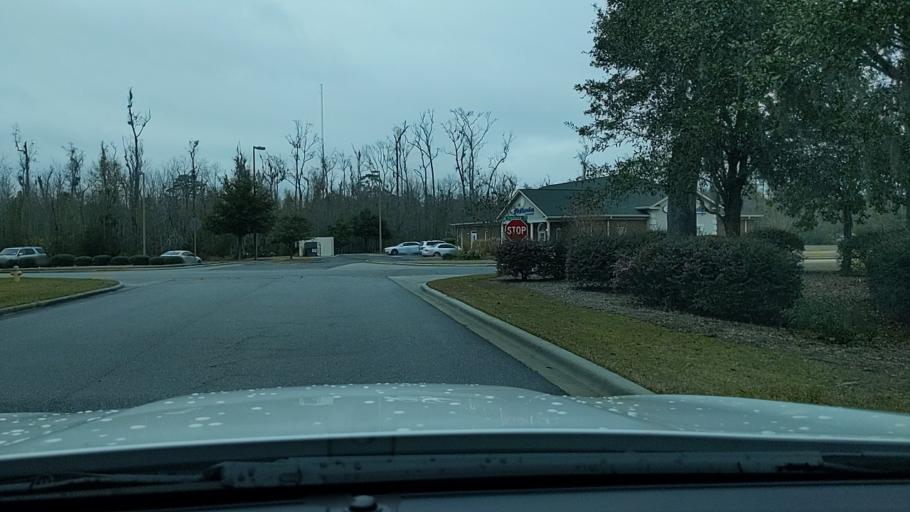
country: US
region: Georgia
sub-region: Chatham County
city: Garden City
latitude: 32.0618
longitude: -81.1556
